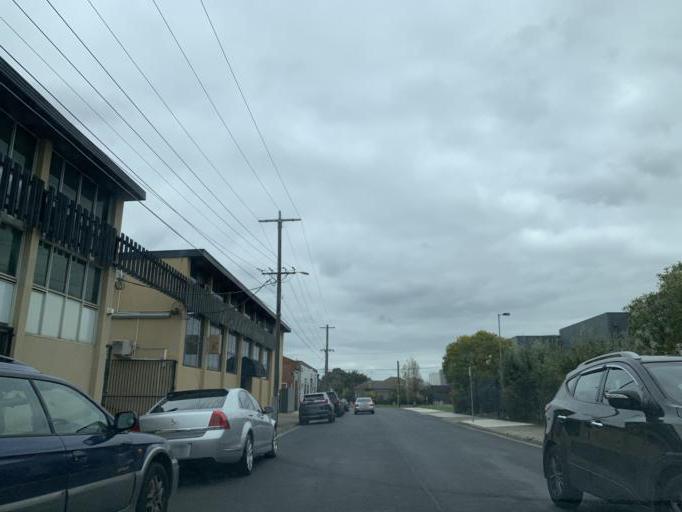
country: AU
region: Victoria
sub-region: Moreland
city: Coburg North
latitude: -37.7301
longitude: 144.9509
